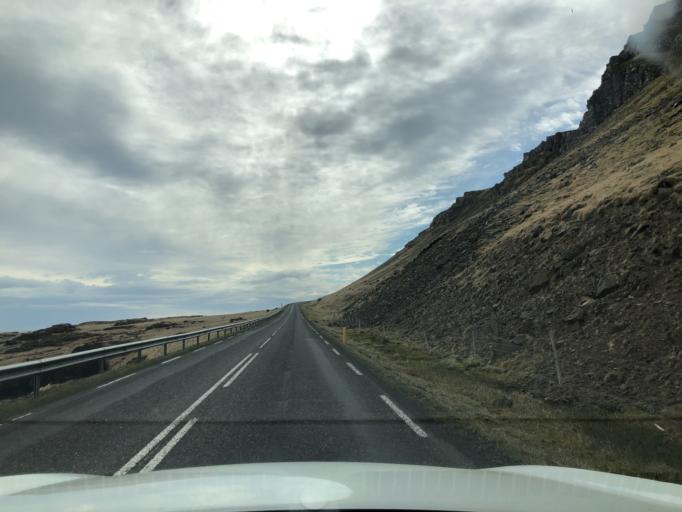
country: IS
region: East
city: Eskifjoerdur
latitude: 64.7408
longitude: -13.9991
